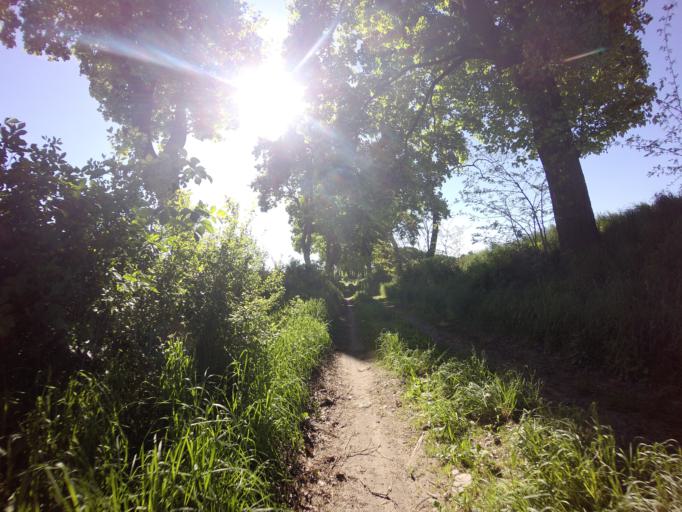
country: PL
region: West Pomeranian Voivodeship
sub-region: Powiat stargardzki
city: Dolice
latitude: 53.1576
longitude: 15.2985
